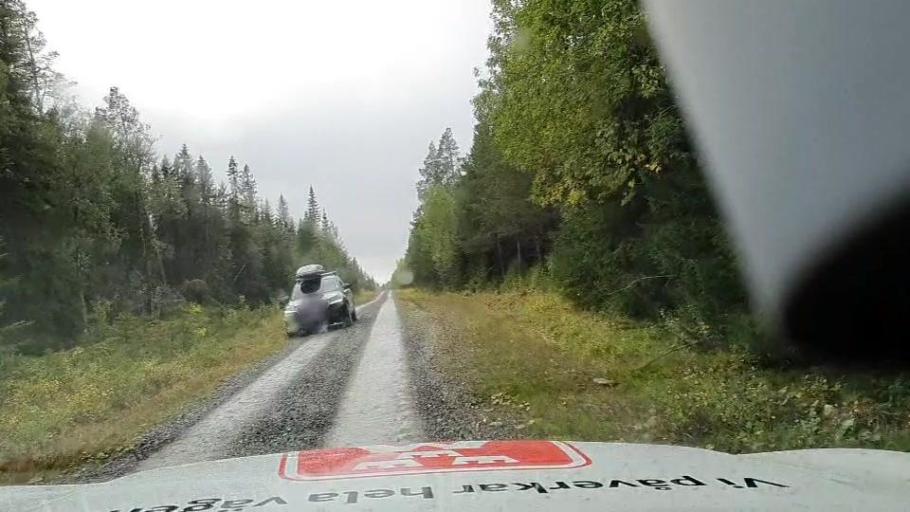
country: SE
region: Jaemtland
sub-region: Are Kommun
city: Jarpen
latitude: 63.2049
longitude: 13.2861
